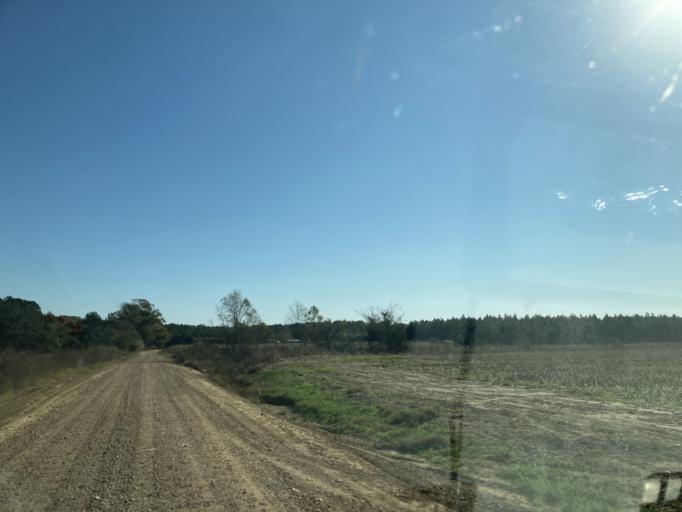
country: US
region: Mississippi
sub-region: Madison County
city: Kearney Park
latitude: 32.7167
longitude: -90.2970
